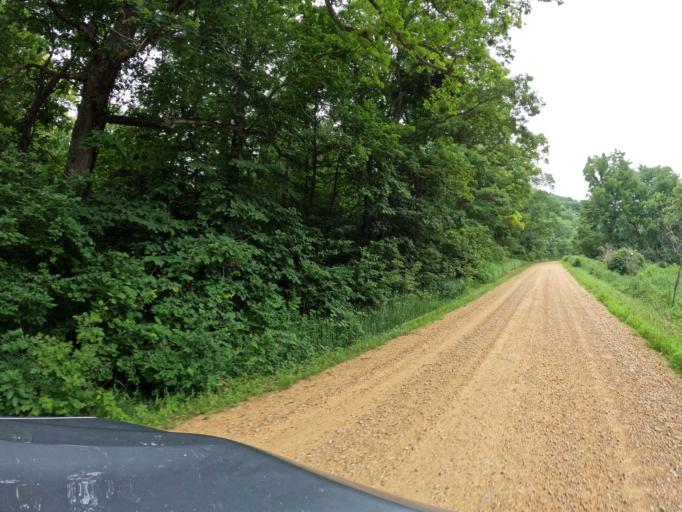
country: US
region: Illinois
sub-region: Carroll County
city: Savanna
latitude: 41.9899
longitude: -90.1744
